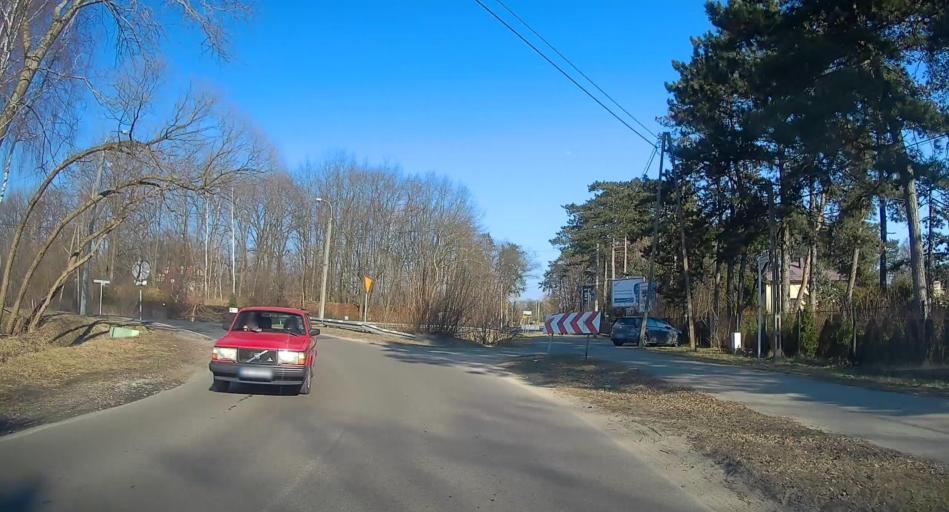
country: PL
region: Masovian Voivodeship
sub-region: Powiat piaseczynski
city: Jozefoslaw
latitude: 52.0824
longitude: 21.0505
